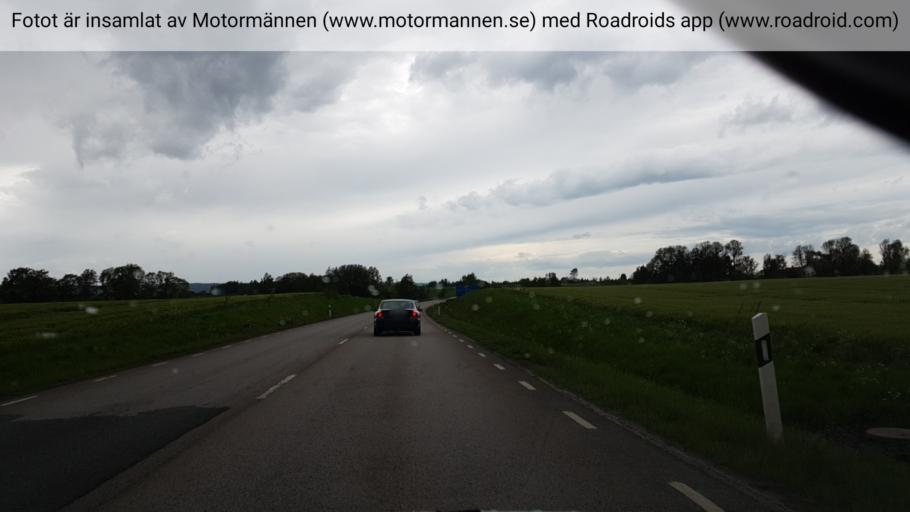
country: SE
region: Vaestra Goetaland
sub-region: Skovde Kommun
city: Skoevde
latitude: 58.3921
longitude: 13.9312
